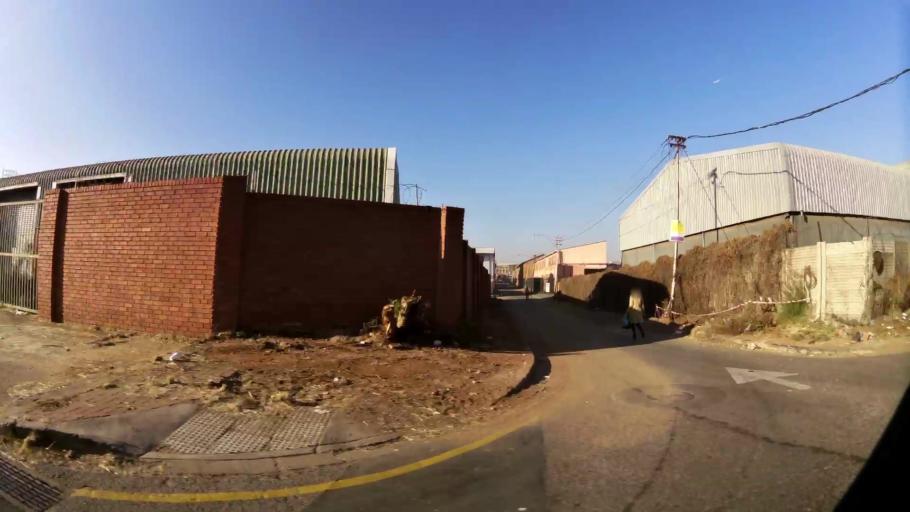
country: ZA
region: Gauteng
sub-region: City of Johannesburg Metropolitan Municipality
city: Johannesburg
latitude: -26.2279
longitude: 28.0254
